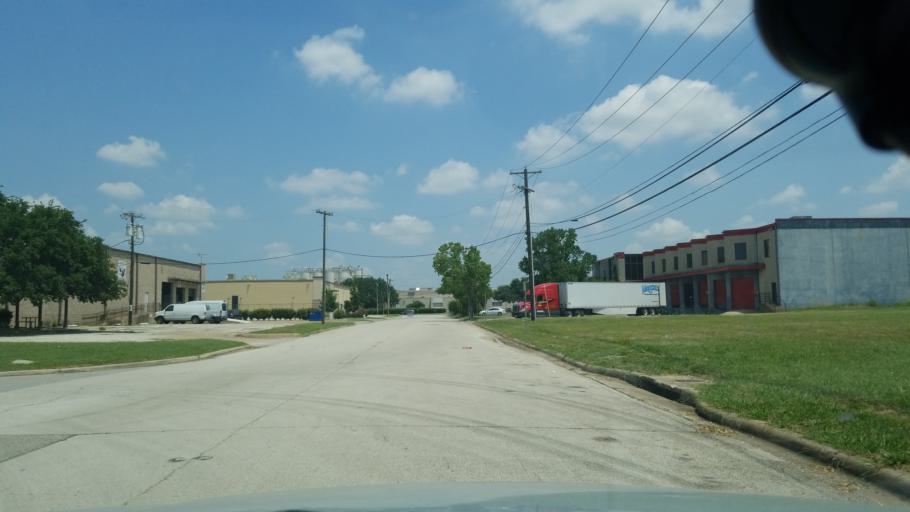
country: US
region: Texas
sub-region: Dallas County
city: Carrollton
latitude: 32.9513
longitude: -96.8633
